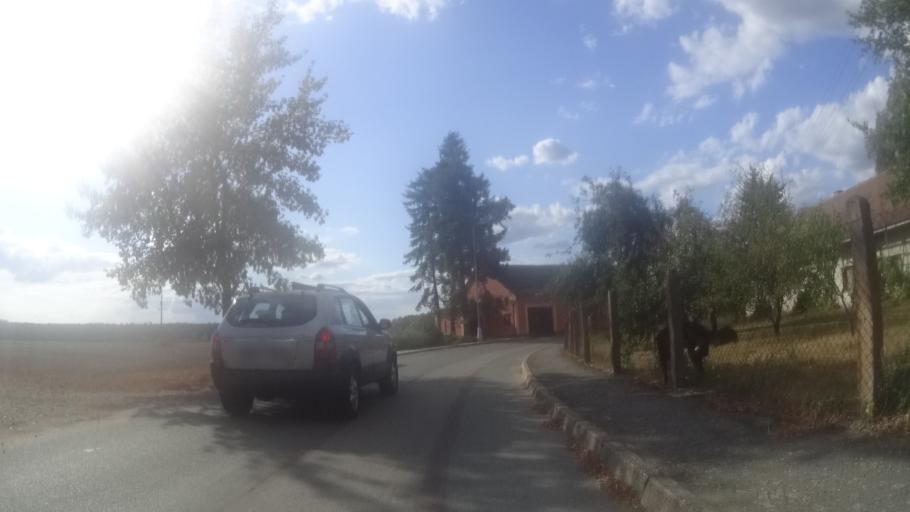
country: CZ
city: Albrechtice nad Orlici
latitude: 50.1485
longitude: 16.0592
